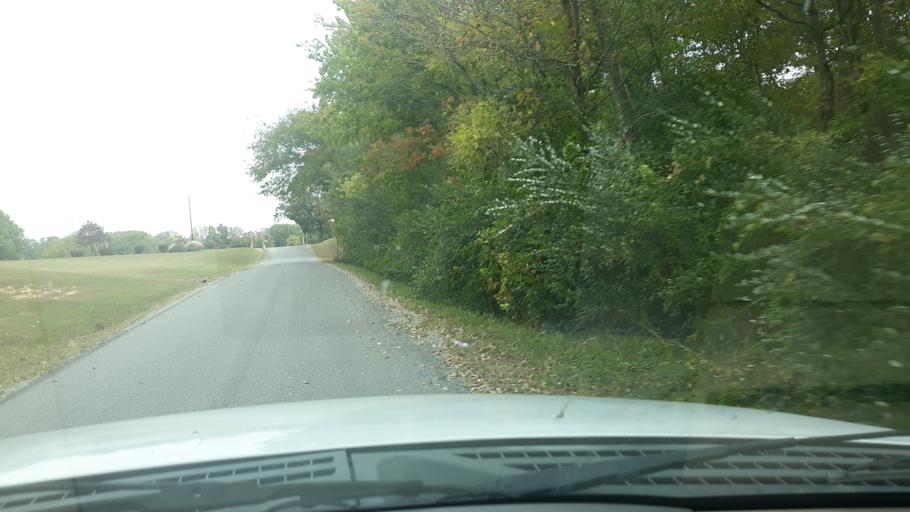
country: US
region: Illinois
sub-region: Saline County
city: Eldorado
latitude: 37.8325
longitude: -88.4849
